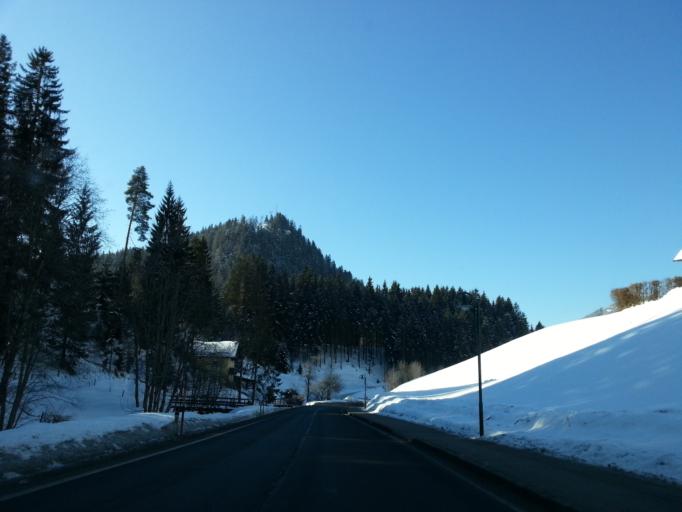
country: AT
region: Salzburg
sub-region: Politischer Bezirk Sankt Johann im Pongau
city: Eben im Pongau
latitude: 47.4586
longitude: 13.3747
